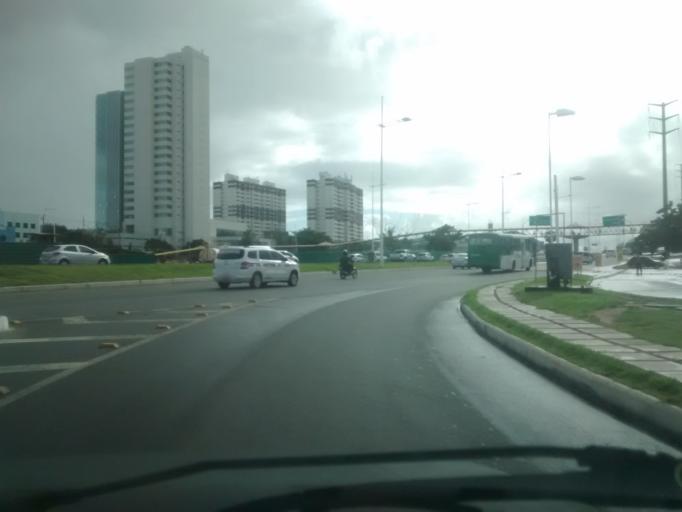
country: BR
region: Bahia
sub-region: Salvador
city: Salvador
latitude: -12.9686
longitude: -38.4389
